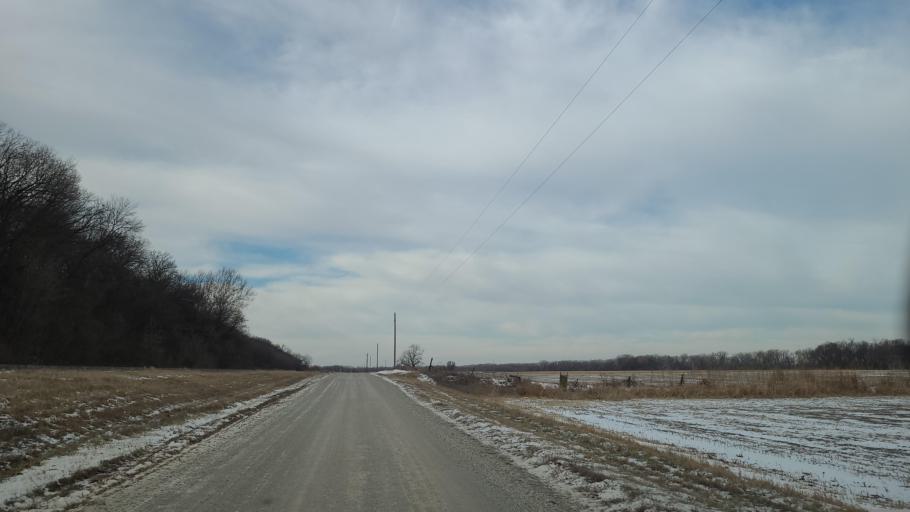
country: US
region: Kansas
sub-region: Jefferson County
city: Oskaloosa
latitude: 39.0611
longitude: -95.4414
